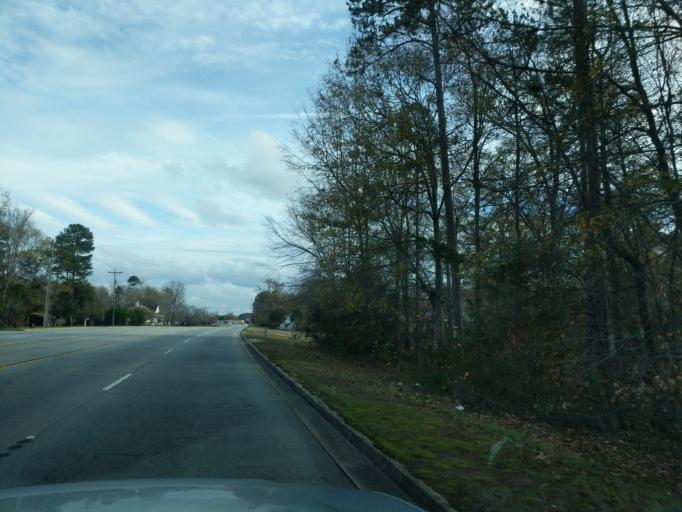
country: US
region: South Carolina
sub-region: Anderson County
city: Honea Path
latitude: 34.5050
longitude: -82.2954
